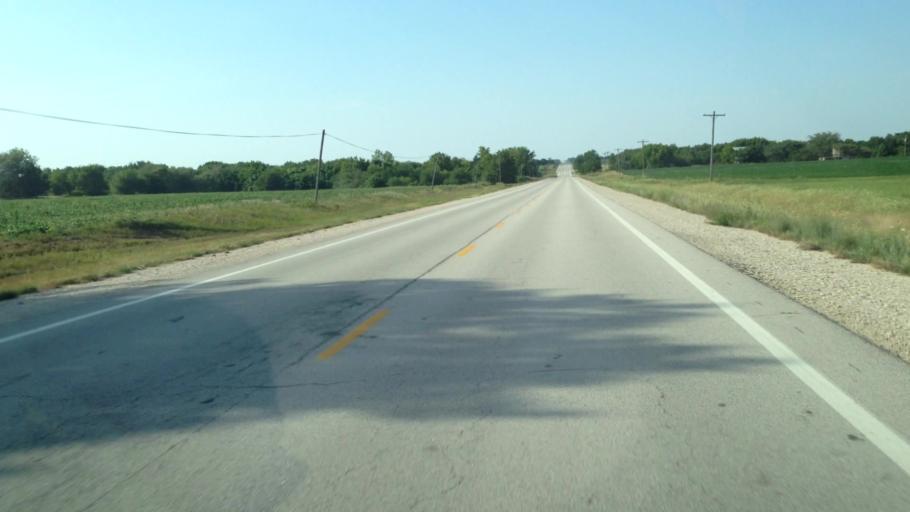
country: US
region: Kansas
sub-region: Anderson County
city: Garnett
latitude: 38.1034
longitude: -95.2429
